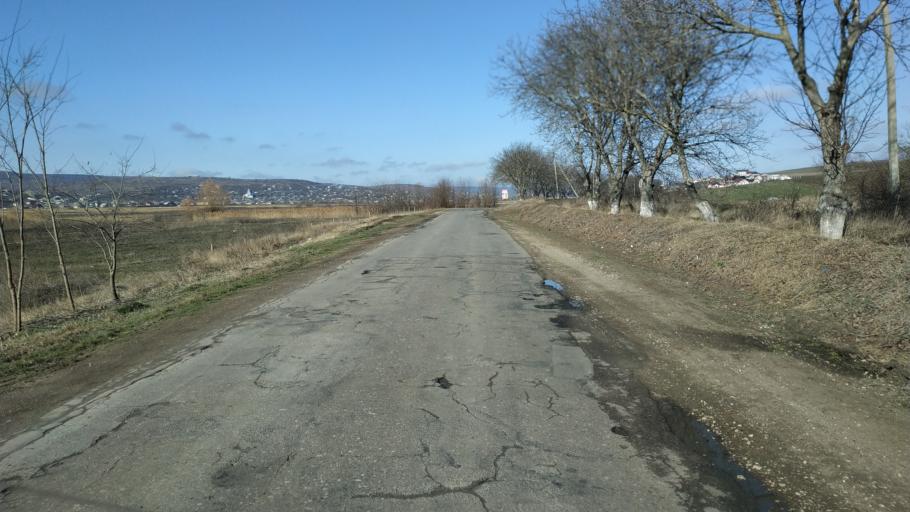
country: MD
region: Laloveni
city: Ialoveni
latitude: 46.9250
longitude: 28.6813
